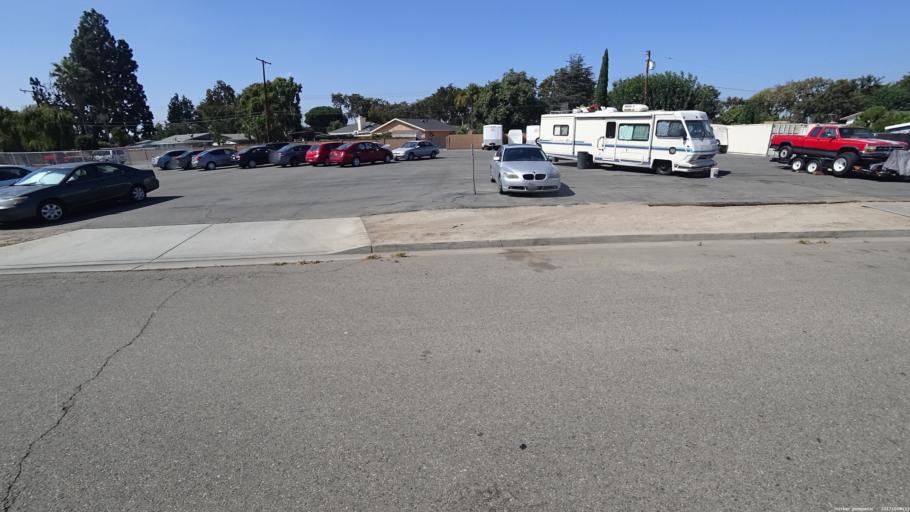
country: US
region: California
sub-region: Orange County
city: Garden Grove
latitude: 33.7900
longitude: -117.9538
